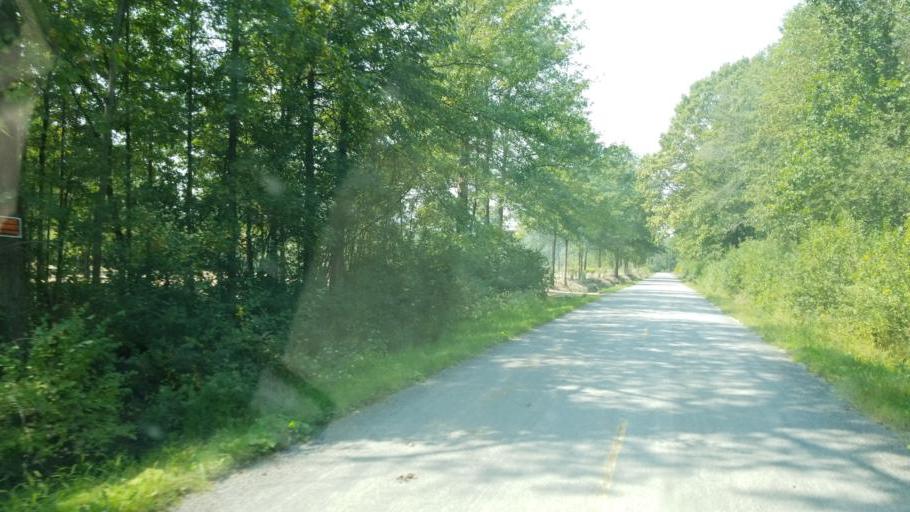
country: US
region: Ohio
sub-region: Ashtabula County
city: Orwell
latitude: 41.4756
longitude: -80.9114
